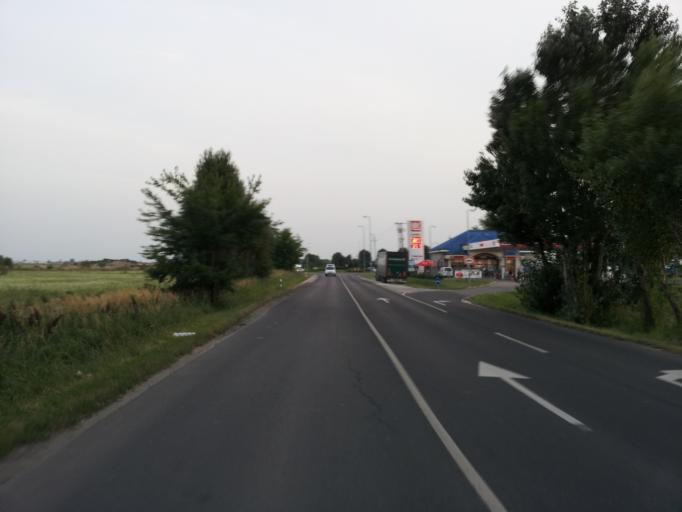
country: HU
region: Pest
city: Szigetszentmiklos
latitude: 47.3715
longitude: 19.0486
